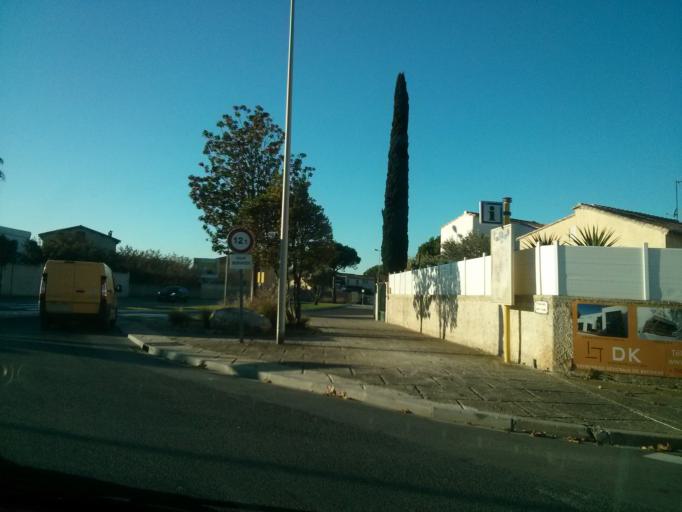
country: FR
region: Languedoc-Roussillon
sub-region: Departement de l'Herault
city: Lunel
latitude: 43.6742
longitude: 4.1451
